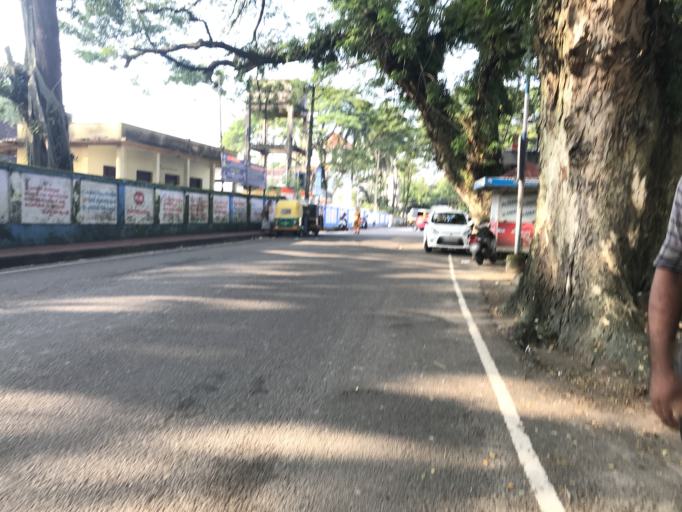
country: IN
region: Kerala
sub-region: Ernakulam
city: Cochin
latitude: 9.9655
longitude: 76.2455
